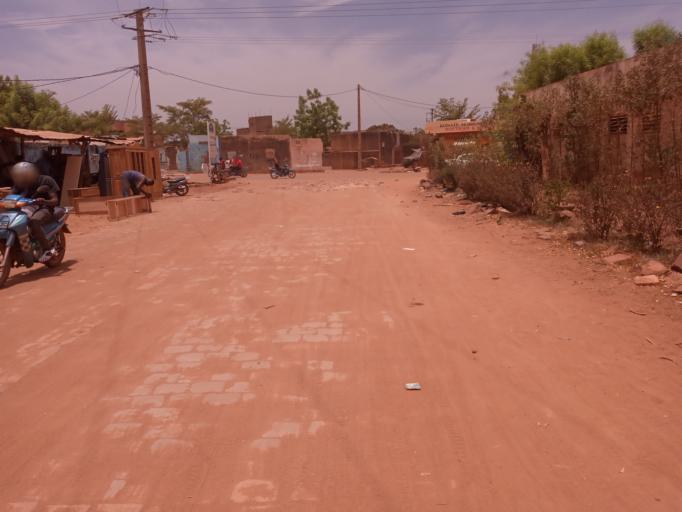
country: ML
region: Bamako
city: Bamako
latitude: 12.5876
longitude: -7.9577
